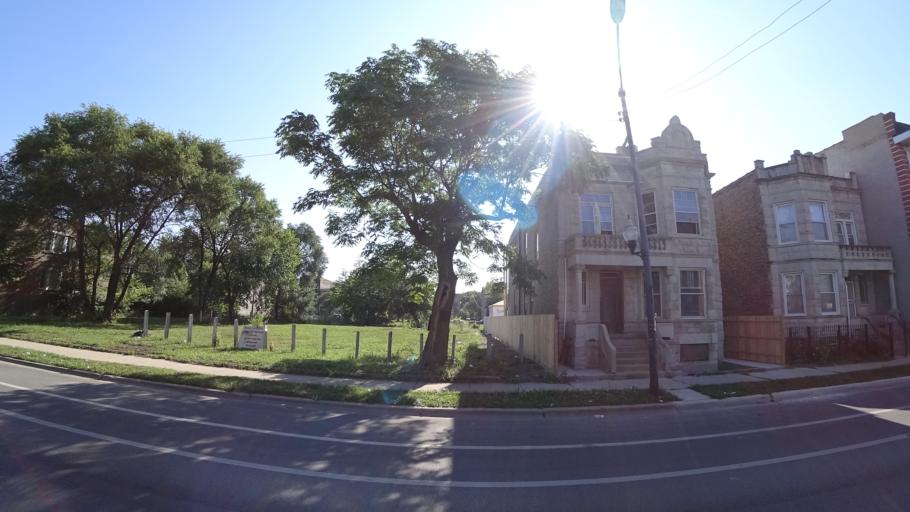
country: US
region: Illinois
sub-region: Cook County
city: Cicero
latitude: 41.8612
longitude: -87.7153
